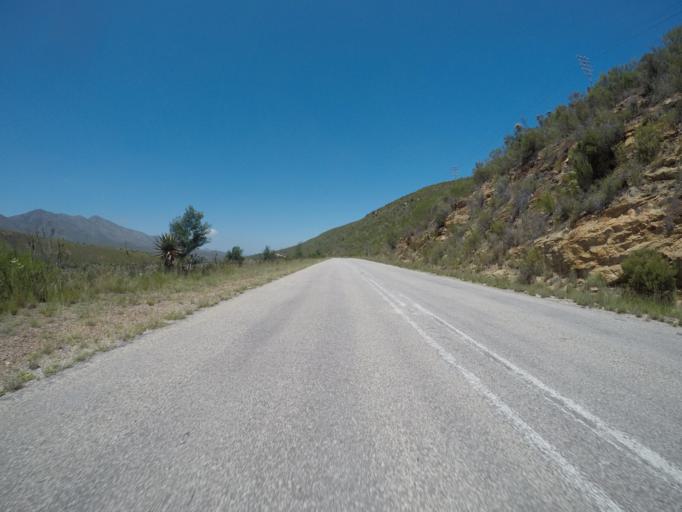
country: ZA
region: Eastern Cape
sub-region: Cacadu District Municipality
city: Kareedouw
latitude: -33.9039
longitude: 24.1362
